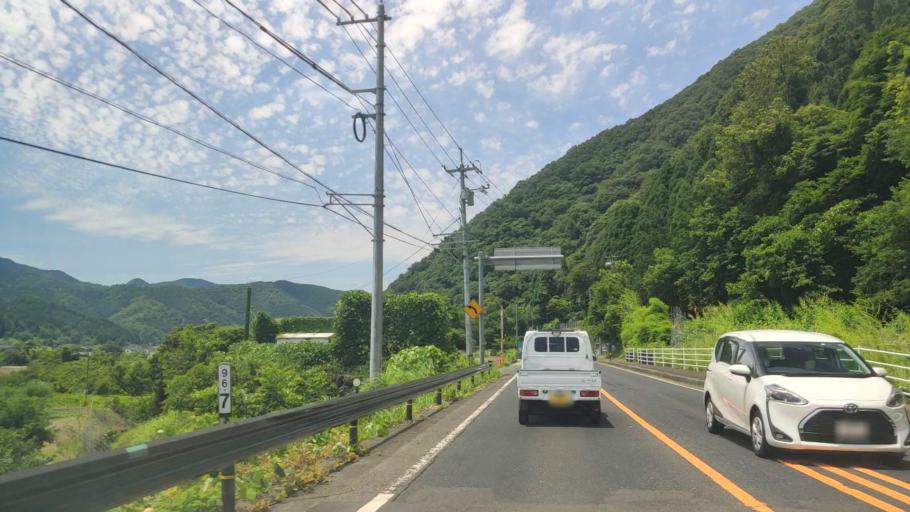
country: JP
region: Tottori
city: Tottori
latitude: 35.3673
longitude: 134.3301
